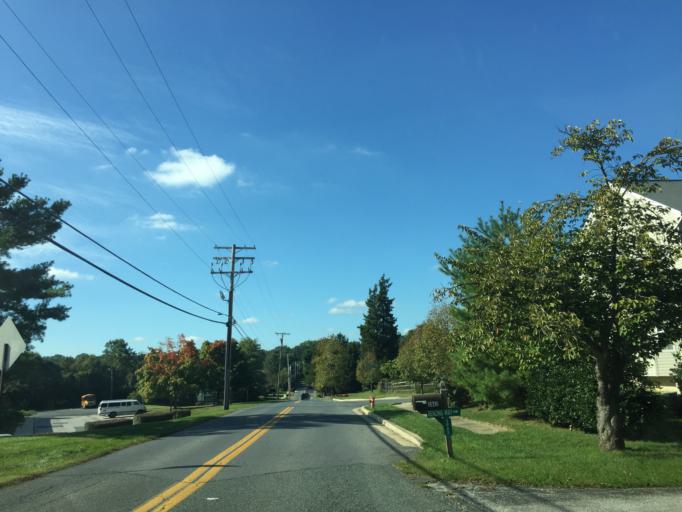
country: US
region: Maryland
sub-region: Baltimore County
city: Perry Hall
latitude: 39.4211
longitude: -76.4617
